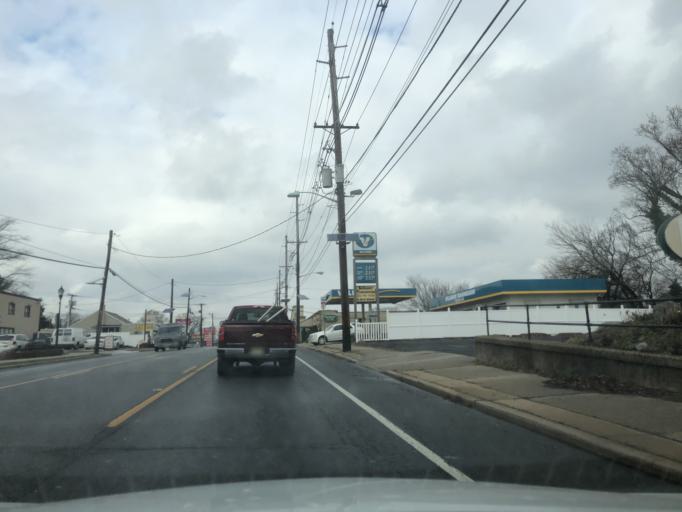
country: US
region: New Jersey
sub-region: Camden County
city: Bellmawr
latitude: 39.8684
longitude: -75.0803
